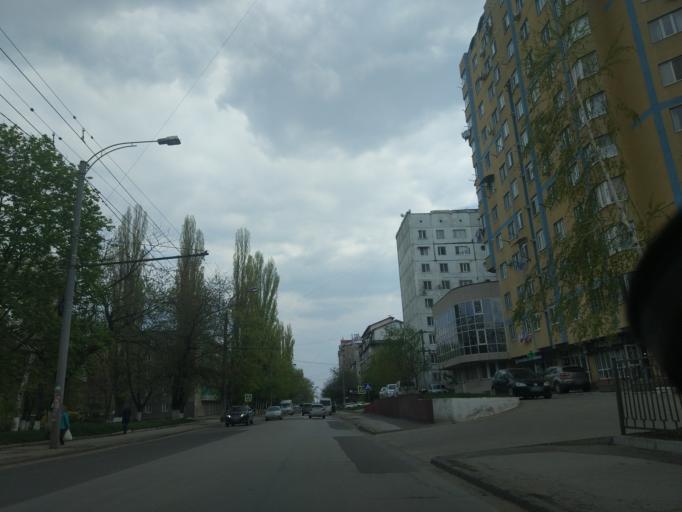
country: MD
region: Chisinau
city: Chisinau
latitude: 46.9881
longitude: 28.8713
